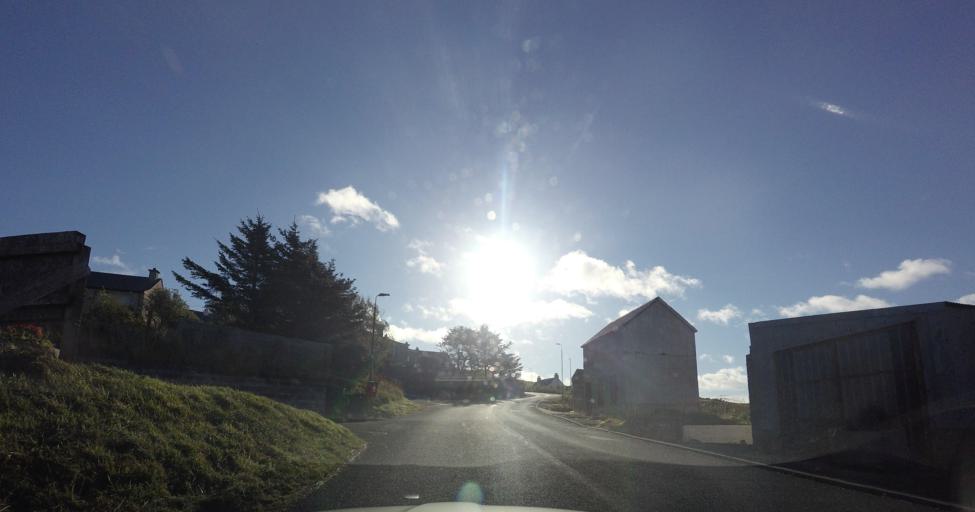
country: GB
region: Scotland
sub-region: Aberdeenshire
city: Macduff
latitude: 57.6705
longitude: -2.3370
